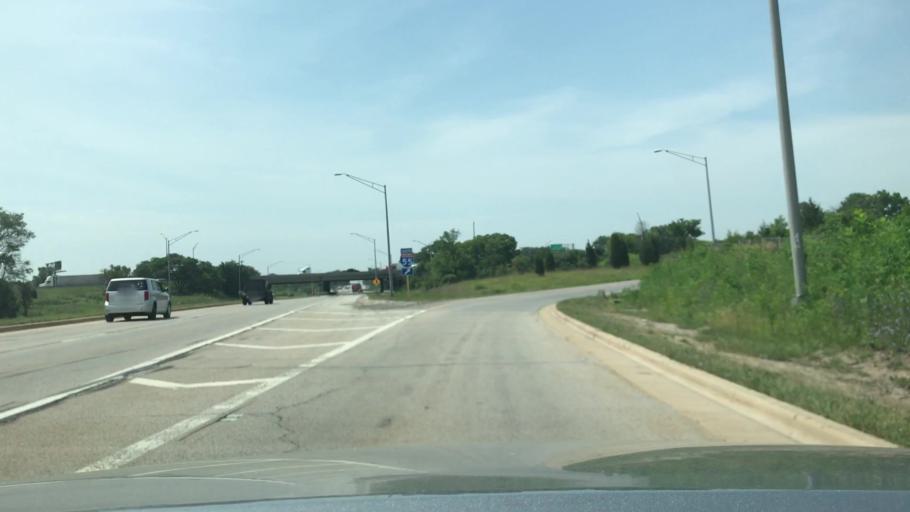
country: US
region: Illinois
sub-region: Cook County
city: Lemont
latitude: 41.7195
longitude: -88.0071
